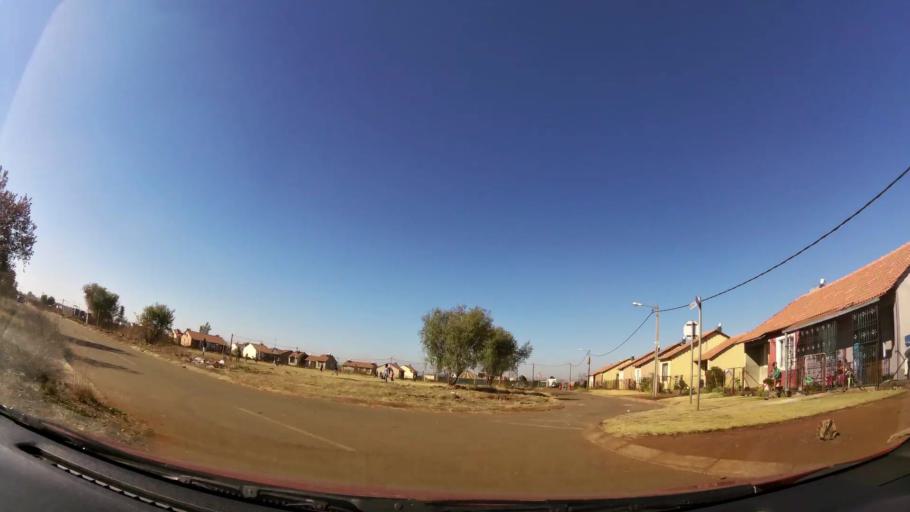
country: ZA
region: Gauteng
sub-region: City of Johannesburg Metropolitan Municipality
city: Soweto
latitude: -26.2412
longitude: 27.8006
